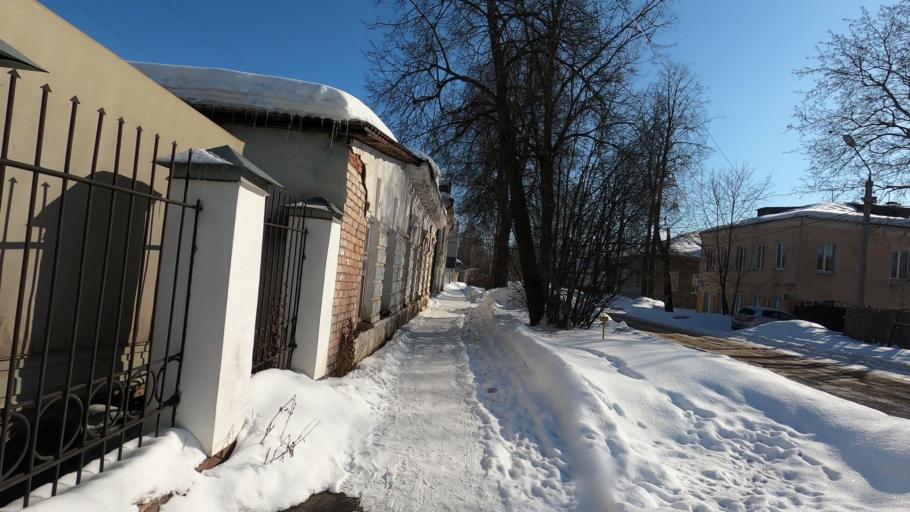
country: RU
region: Jaroslavl
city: Rybinsk
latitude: 58.0460
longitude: 38.8652
